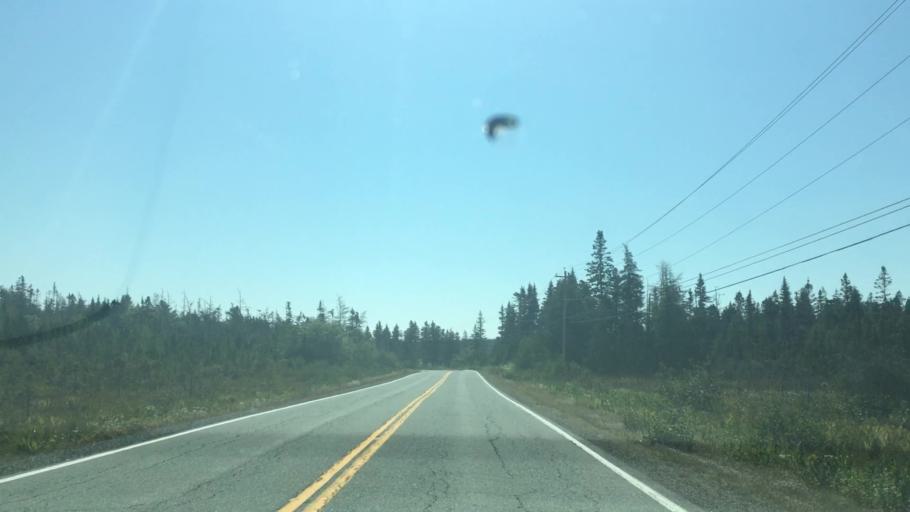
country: CA
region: Nova Scotia
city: Antigonish
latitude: 45.0094
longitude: -62.0905
